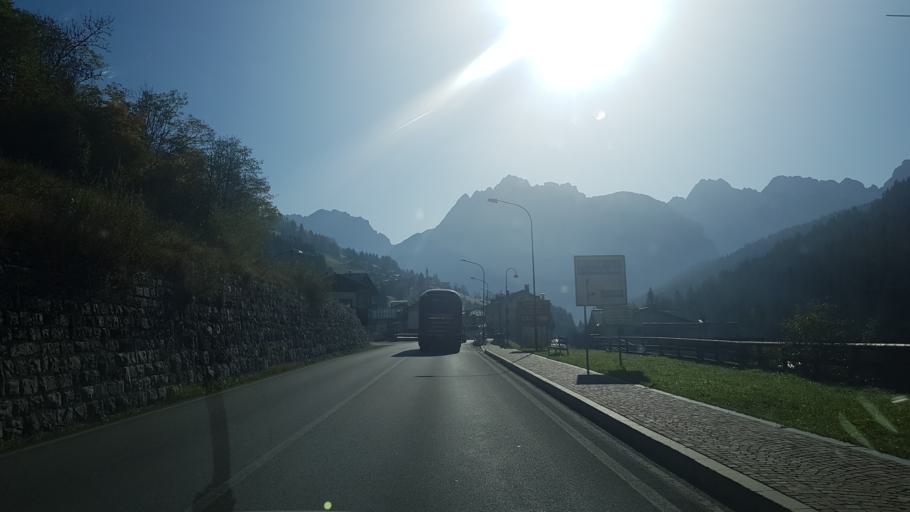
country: IT
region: Veneto
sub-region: Provincia di Belluno
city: San Nicolo Comelico
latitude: 46.5789
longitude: 12.5291
